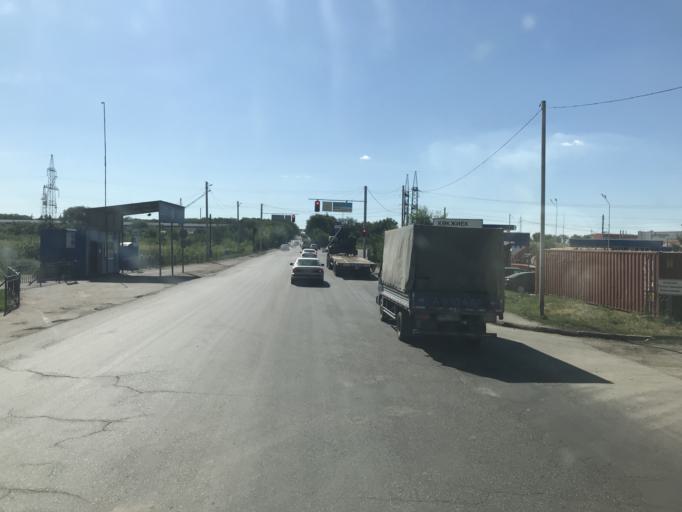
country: KZ
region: Almaty Oblysy
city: Pervomayskiy
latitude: 43.3547
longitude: 76.9160
